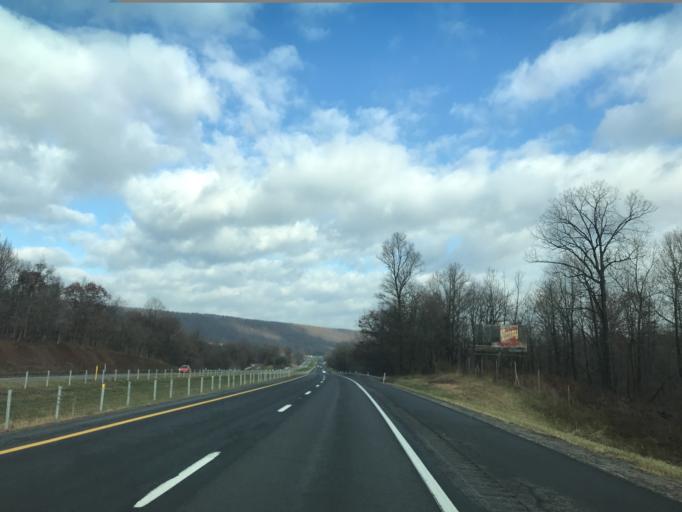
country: US
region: Maryland
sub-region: Washington County
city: Hancock
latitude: 39.8196
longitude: -78.2714
